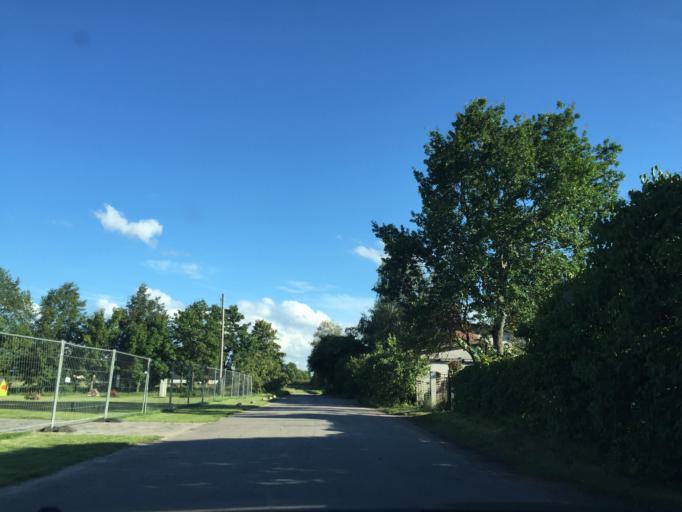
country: LV
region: Riga
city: Jaunciems
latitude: 57.0604
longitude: 24.1387
